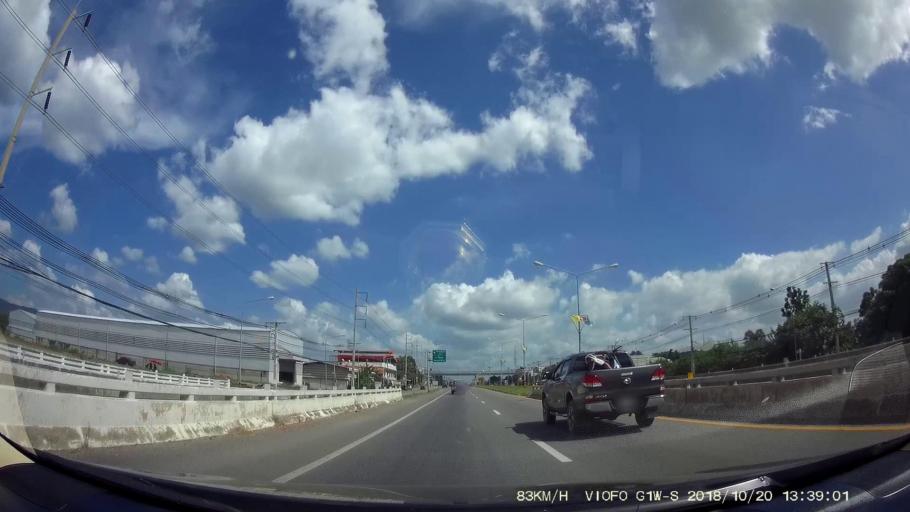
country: TH
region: Khon Kaen
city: Chum Phae
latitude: 16.5501
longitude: 102.0888
